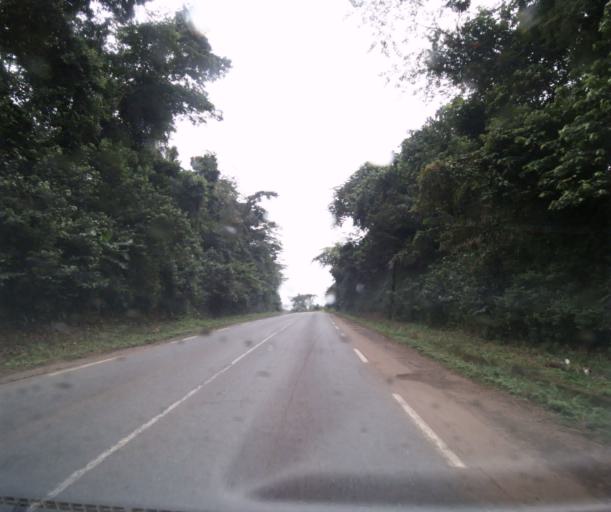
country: CM
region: Centre
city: Mbankomo
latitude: 3.7733
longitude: 11.1534
